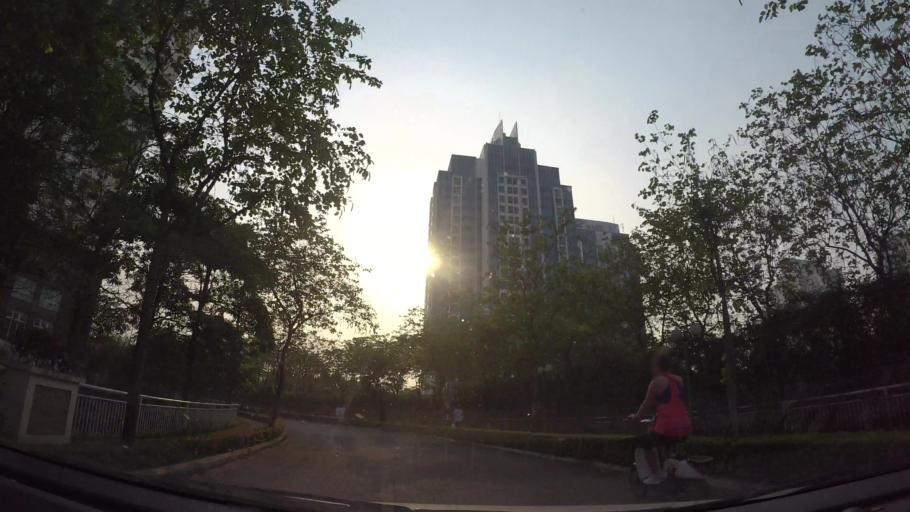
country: VN
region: Ha Noi
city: Tay Ho
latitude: 21.0795
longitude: 105.7932
